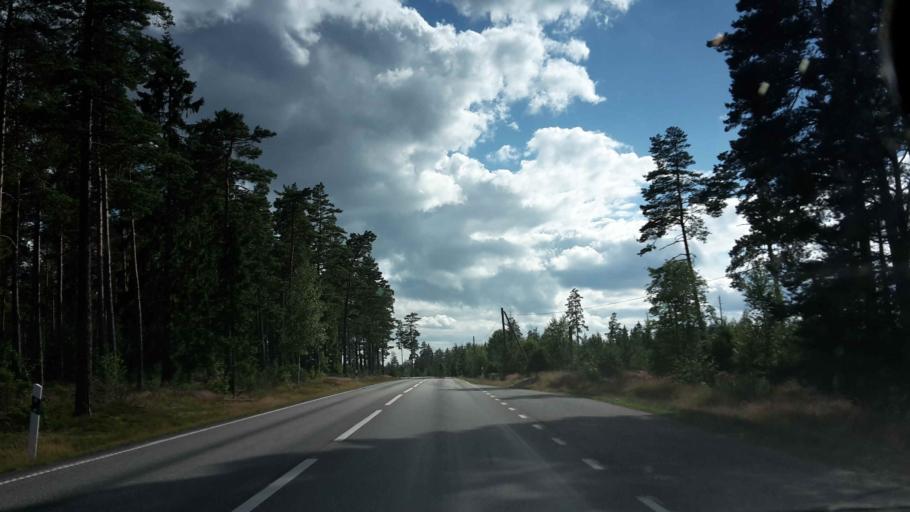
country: SE
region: OErebro
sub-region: Hallsbergs Kommun
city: Palsboda
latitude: 58.8617
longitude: 15.4113
